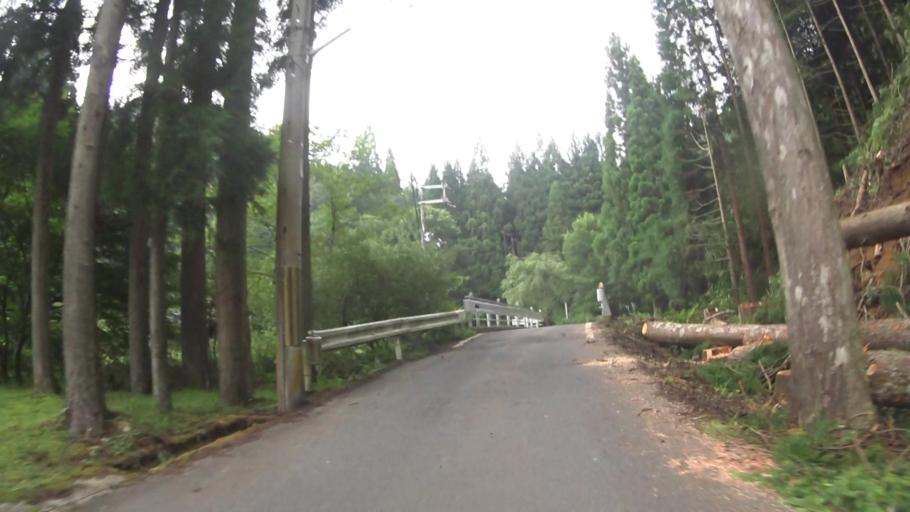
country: JP
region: Shiga Prefecture
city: Kitahama
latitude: 35.2624
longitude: 135.7692
